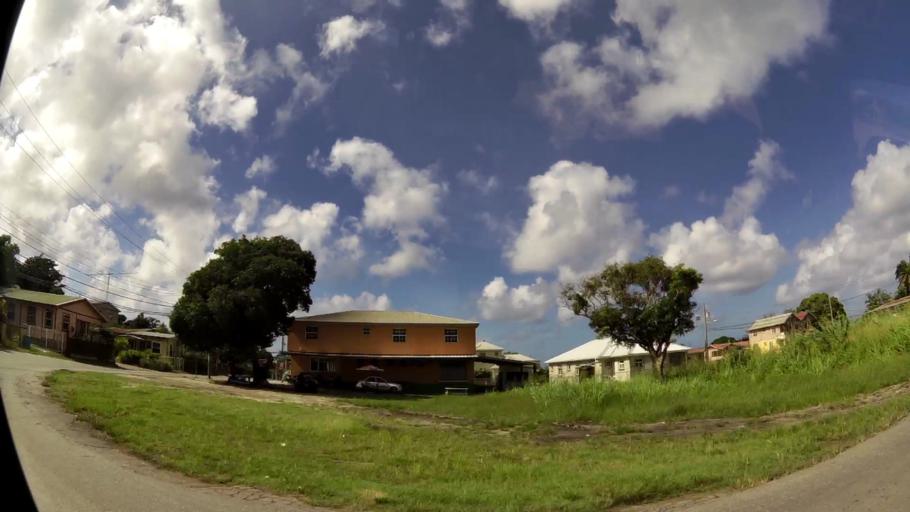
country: BB
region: Saint Lucy
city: Checker Hall
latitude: 13.2834
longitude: -59.6437
